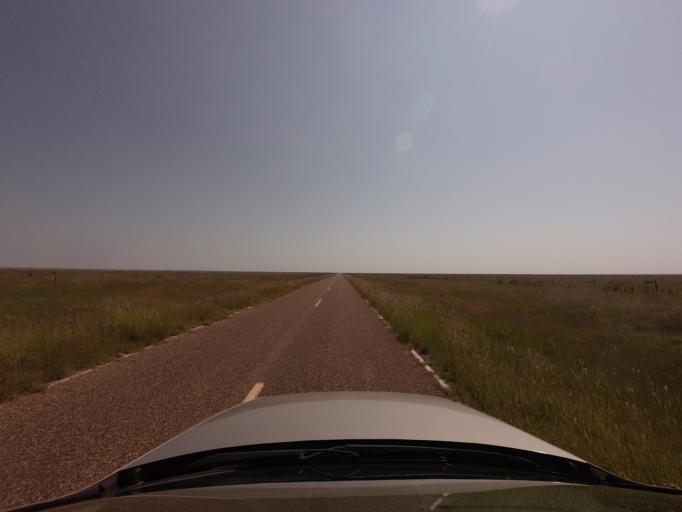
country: US
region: New Mexico
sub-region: Curry County
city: Cannon Air Force Base
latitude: 34.6333
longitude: -103.4419
